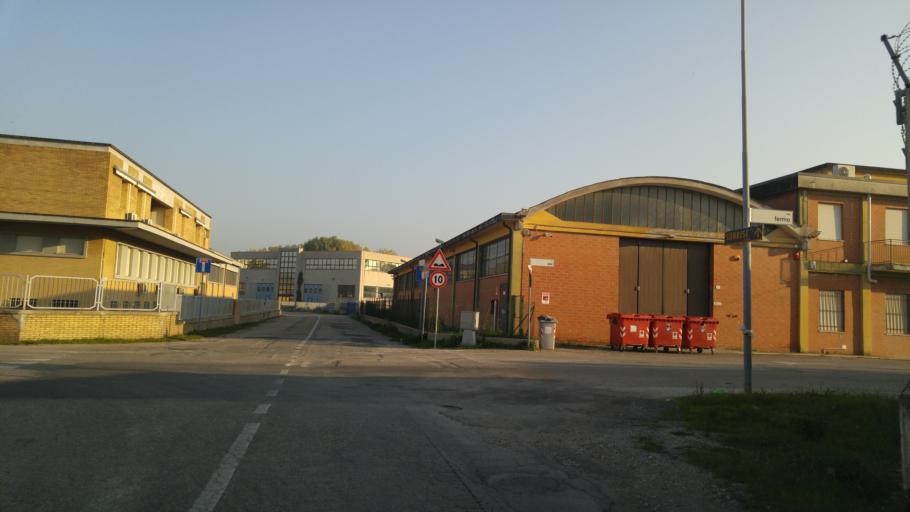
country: IT
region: The Marches
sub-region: Provincia di Pesaro e Urbino
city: Pesaro
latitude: 43.9028
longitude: 12.8851
